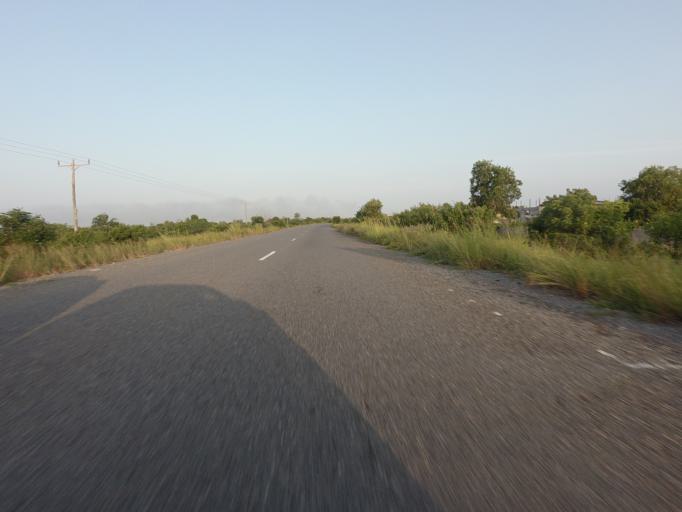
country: GH
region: Volta
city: Anloga
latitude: 5.8451
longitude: 0.7802
